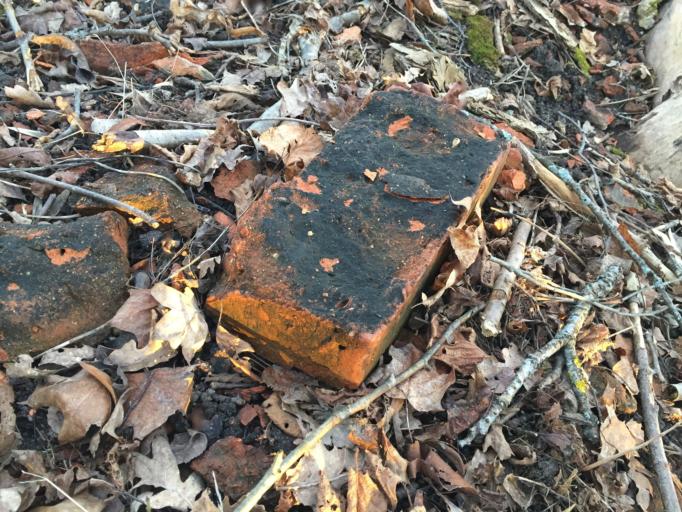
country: SE
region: Stockholm
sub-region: Salems Kommun
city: Ronninge
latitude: 59.2594
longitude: 17.7120
